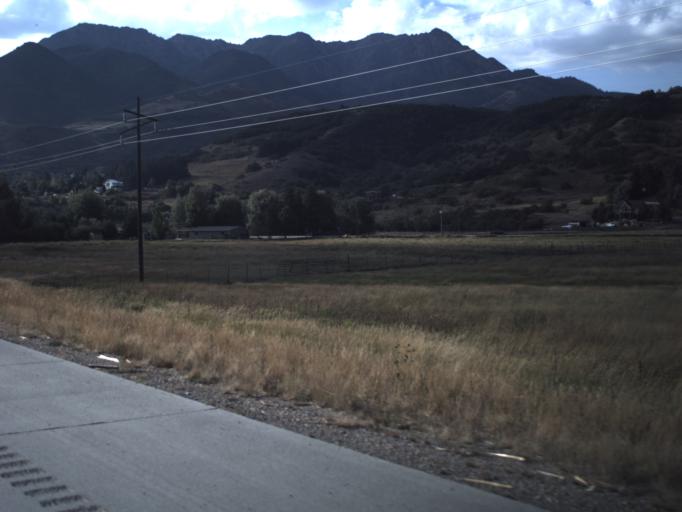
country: US
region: Utah
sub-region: Morgan County
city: Mountain Green
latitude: 41.1392
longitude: -111.8153
